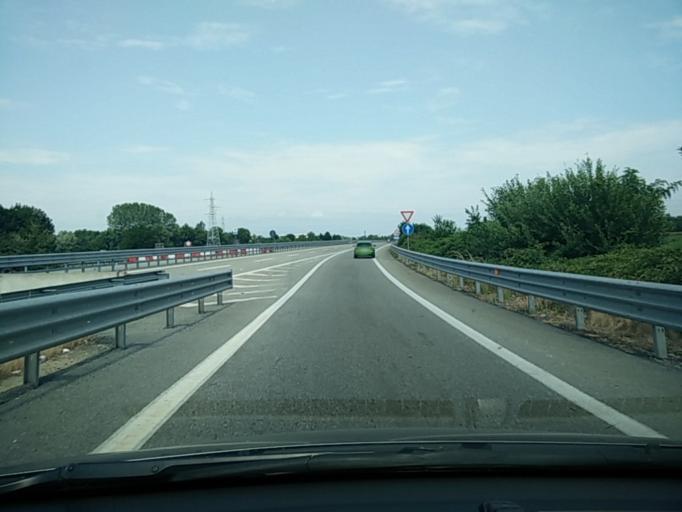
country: IT
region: Piedmont
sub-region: Provincia di Torino
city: Brandizzo
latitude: 45.1732
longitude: 7.8068
